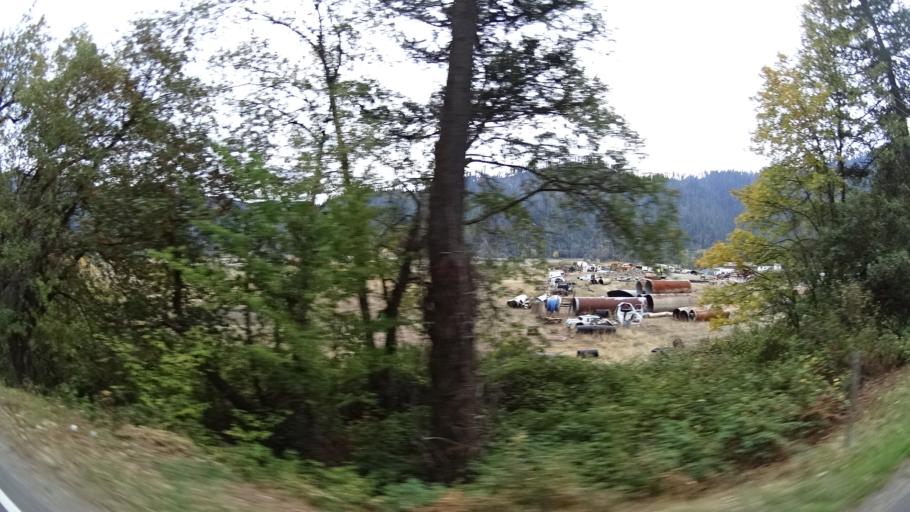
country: US
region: California
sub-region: Siskiyou County
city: Happy Camp
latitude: 41.8008
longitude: -123.3735
